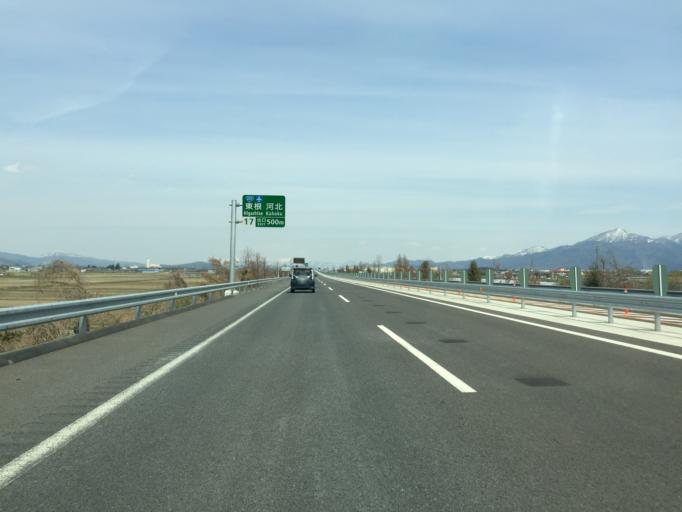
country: JP
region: Yamagata
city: Tendo
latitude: 38.4013
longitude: 140.3441
